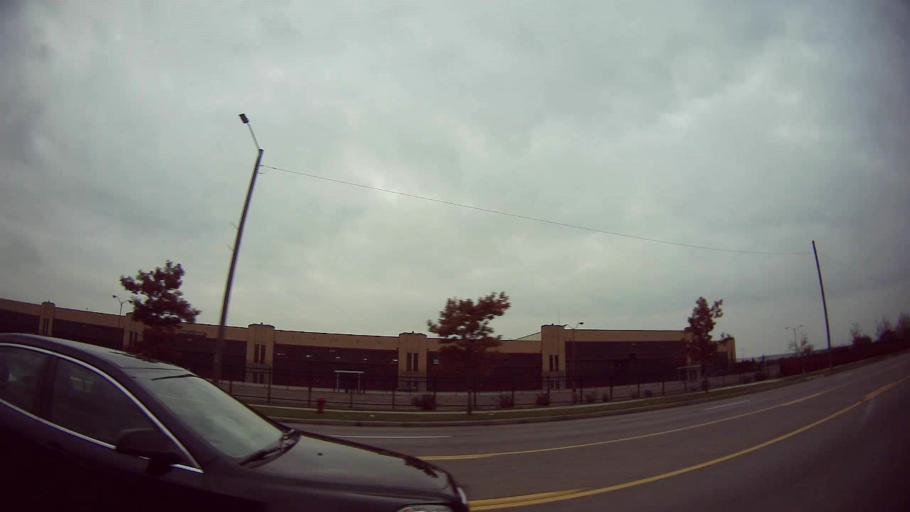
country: US
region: Michigan
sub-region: Wayne County
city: Hamtramck
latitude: 42.4063
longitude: -82.9992
